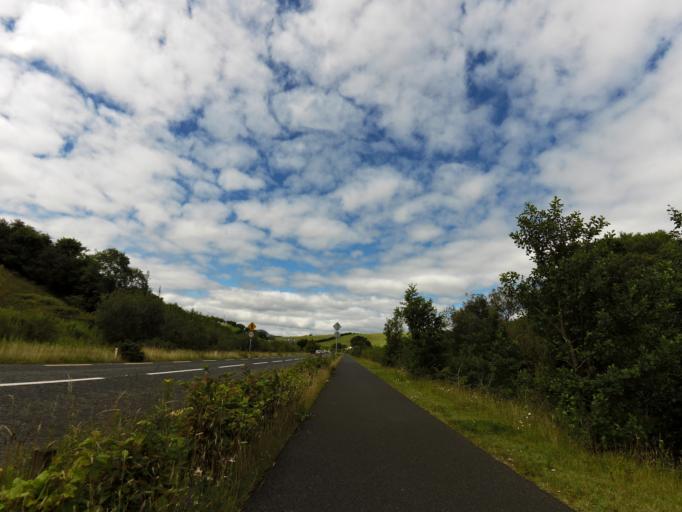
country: IE
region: Connaught
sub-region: Maigh Eo
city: Westport
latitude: 53.8712
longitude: -9.5366
